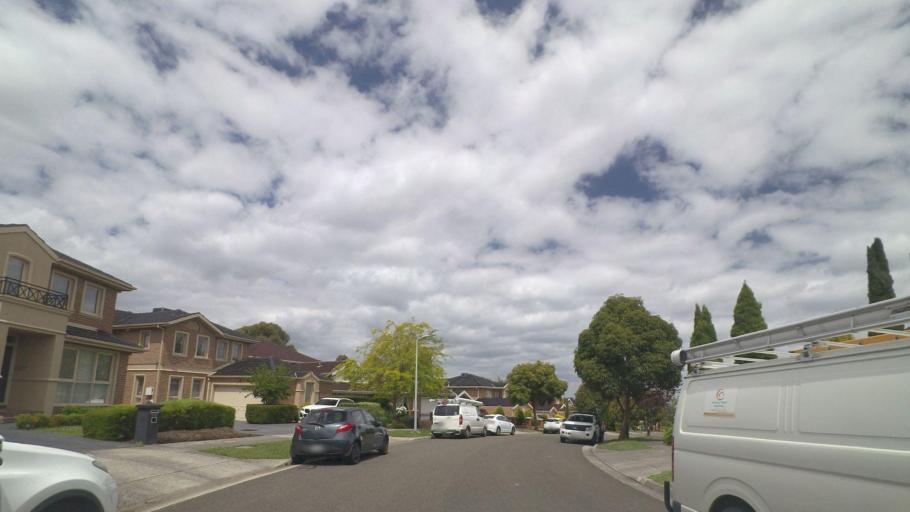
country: AU
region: Victoria
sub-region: Knox
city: Wantirna
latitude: -37.8641
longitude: 145.2175
